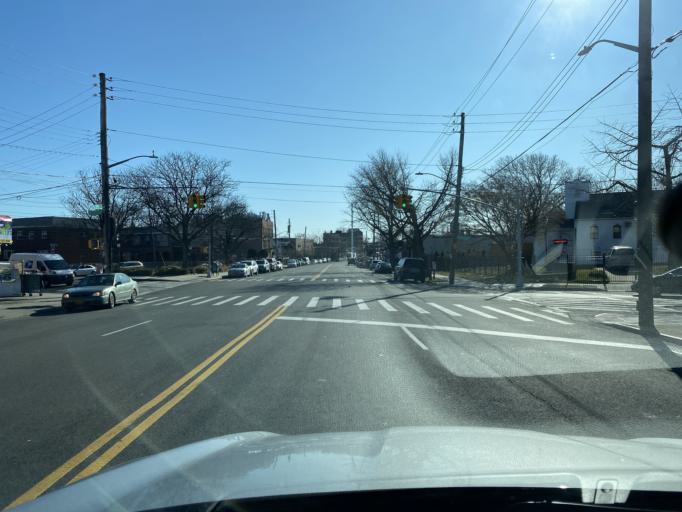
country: US
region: New York
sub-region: Bronx
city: The Bronx
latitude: 40.8136
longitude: -73.8581
